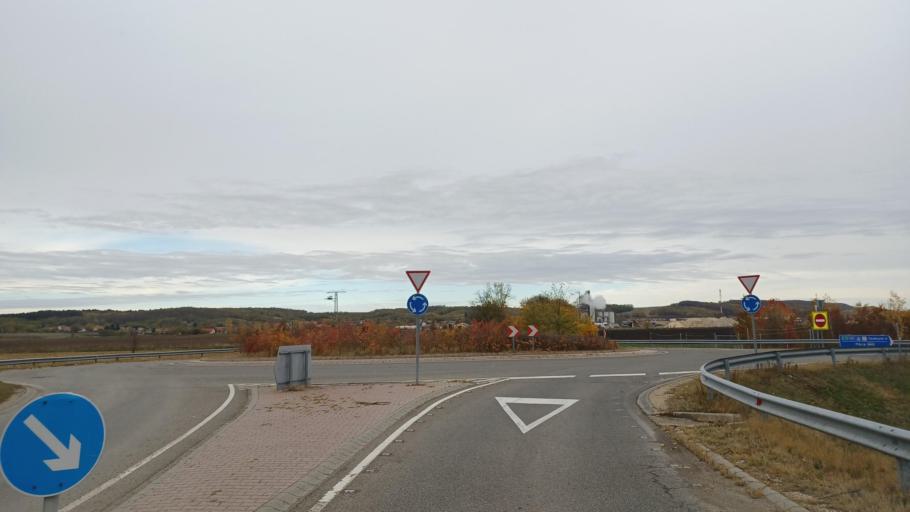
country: HU
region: Tolna
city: Dunaszentgyorgy
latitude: 46.5201
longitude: 18.7760
